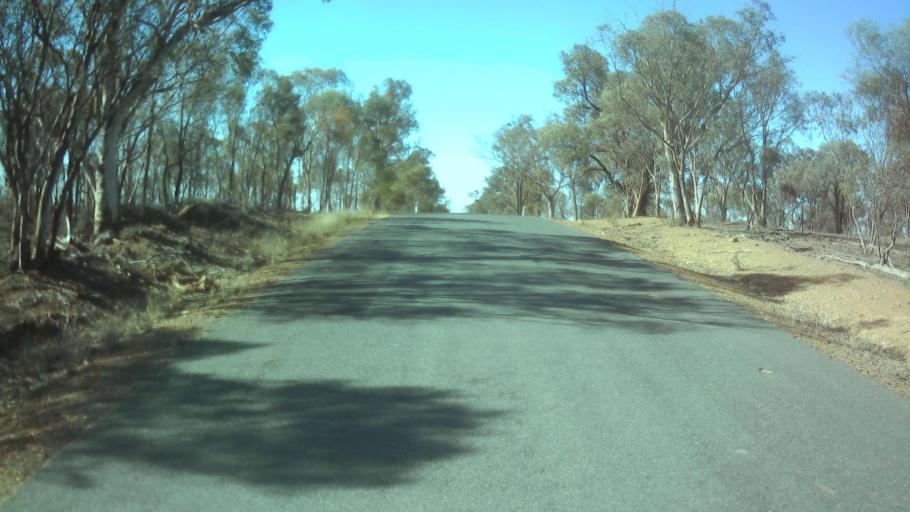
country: AU
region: New South Wales
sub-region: Forbes
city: Forbes
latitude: -33.7052
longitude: 147.8058
